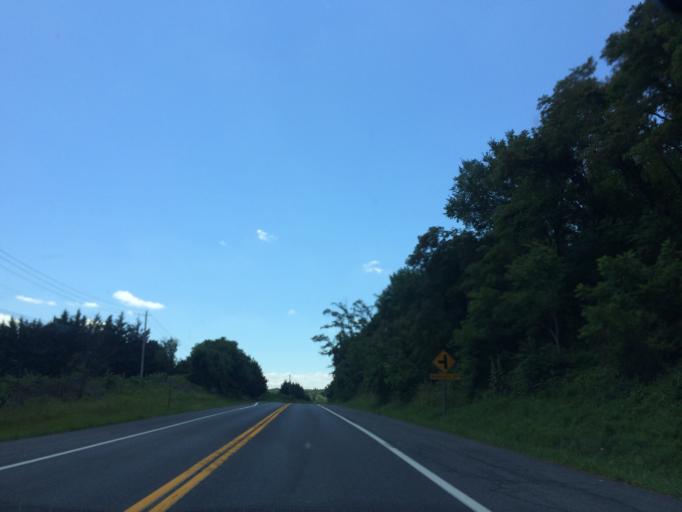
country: US
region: Maryland
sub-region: Frederick County
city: Linganore
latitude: 39.4790
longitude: -77.2013
